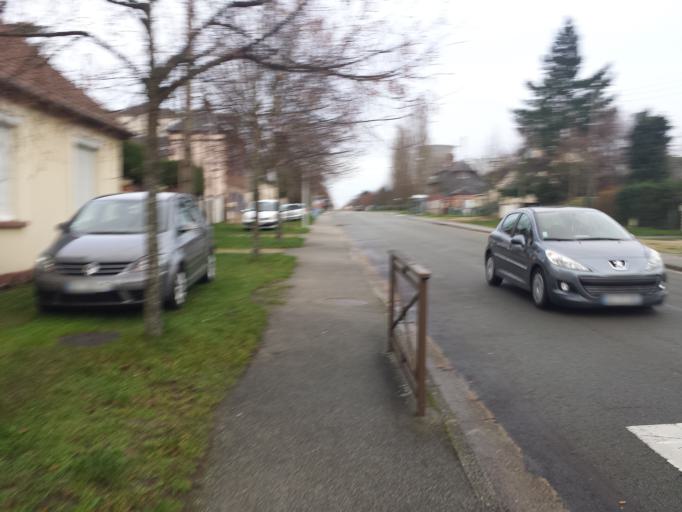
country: FR
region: Haute-Normandie
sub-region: Departement de l'Eure
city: Evreux
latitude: 49.0184
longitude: 1.1656
